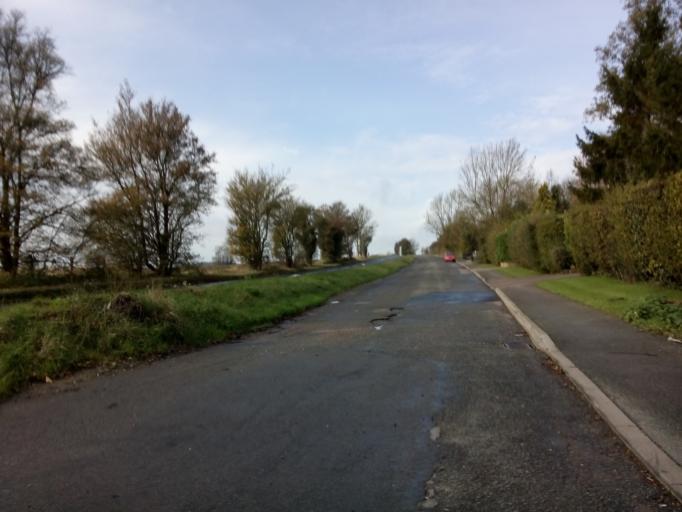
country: GB
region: England
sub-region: Suffolk
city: Needham Market
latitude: 52.1629
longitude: 1.0389
